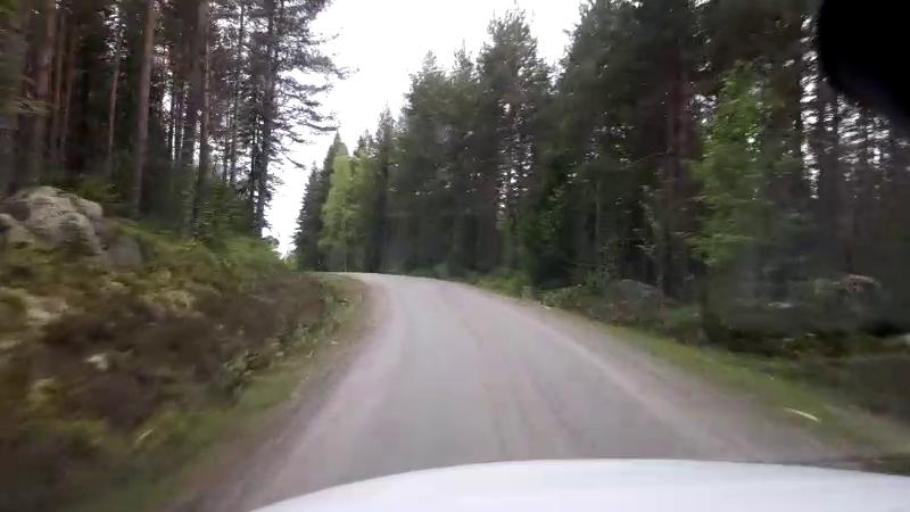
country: SE
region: Gaevleborg
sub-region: Ljusdals Kommun
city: Jaervsoe
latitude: 61.7667
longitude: 16.1858
